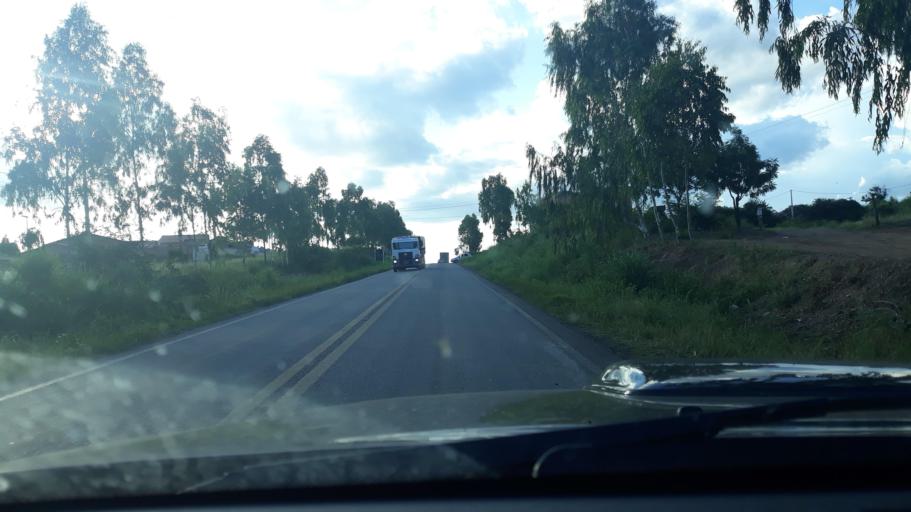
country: BR
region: Bahia
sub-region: Riacho De Santana
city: Riacho de Santana
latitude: -13.7672
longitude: -42.7215
